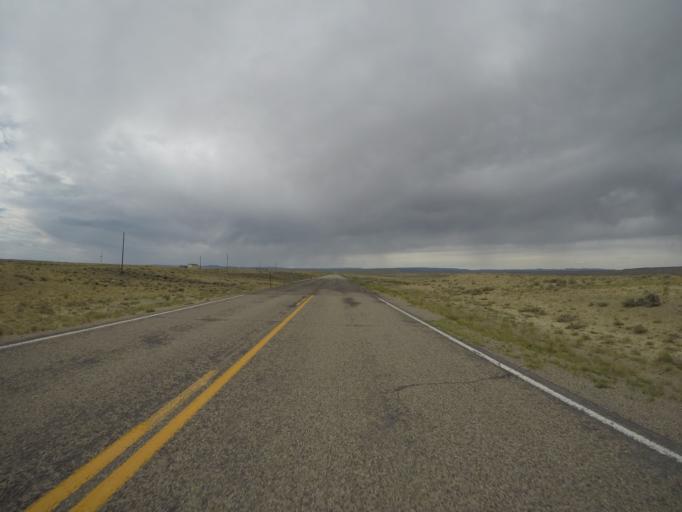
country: US
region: Wyoming
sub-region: Lincoln County
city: Kemmerer
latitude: 41.9631
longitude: -110.1276
